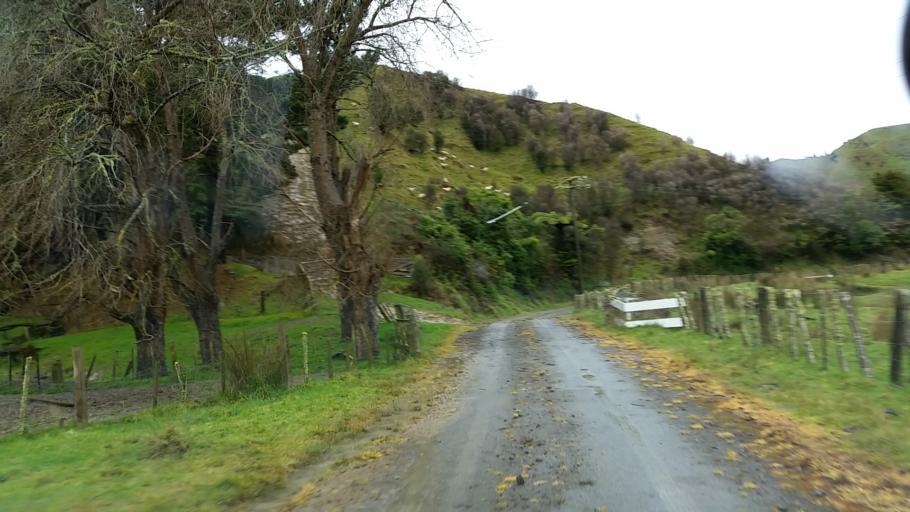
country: NZ
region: Taranaki
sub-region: South Taranaki District
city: Eltham
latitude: -39.4885
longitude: 174.4346
